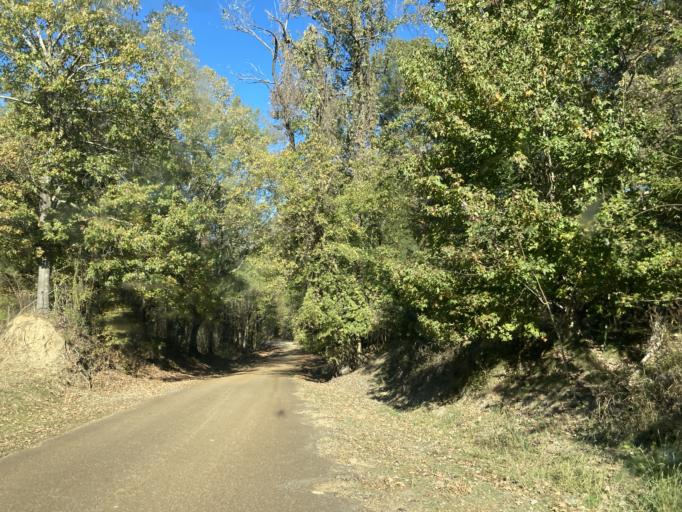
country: US
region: Mississippi
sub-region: Yazoo County
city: Yazoo City
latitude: 32.7174
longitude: -90.3766
